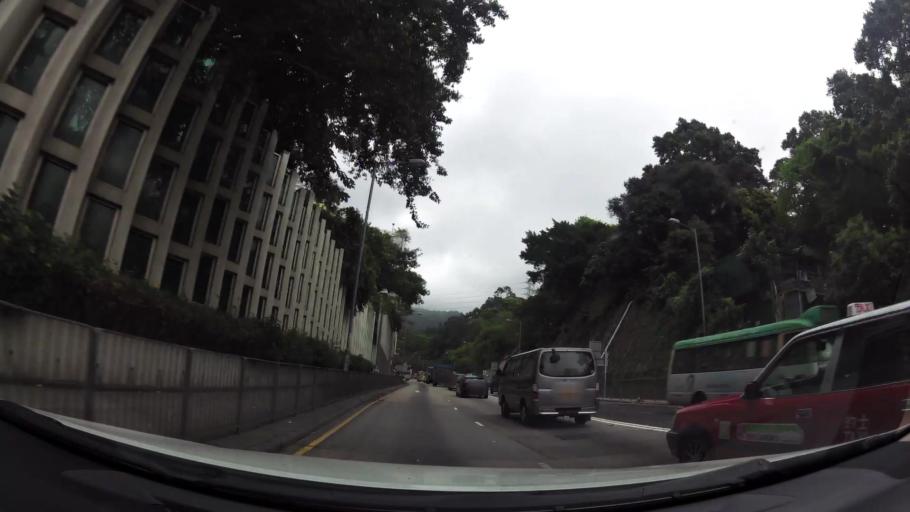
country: HK
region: Tsuen Wan
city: Tsuen Wan
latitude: 22.3767
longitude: 114.1366
